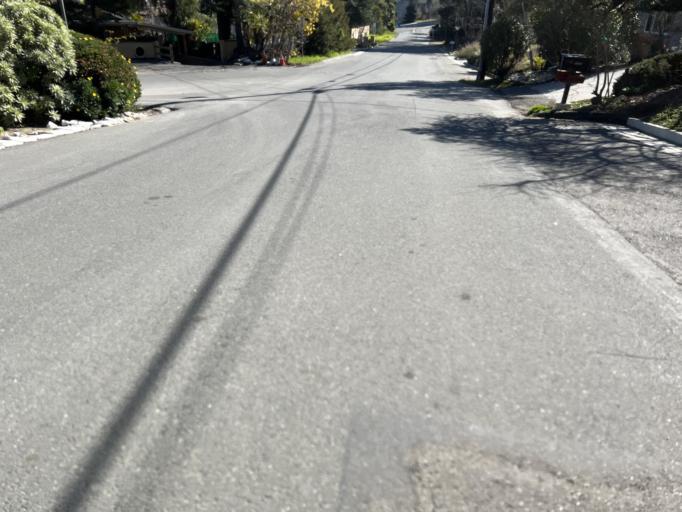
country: US
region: California
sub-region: Santa Clara County
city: Cupertino
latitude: 37.3128
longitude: -122.0704
